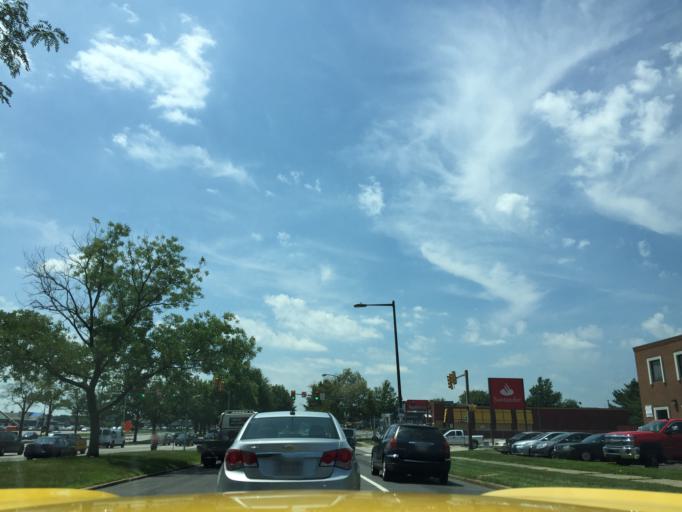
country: US
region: Pennsylvania
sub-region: Montgomery County
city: Rockledge
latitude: 40.0772
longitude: -75.0325
